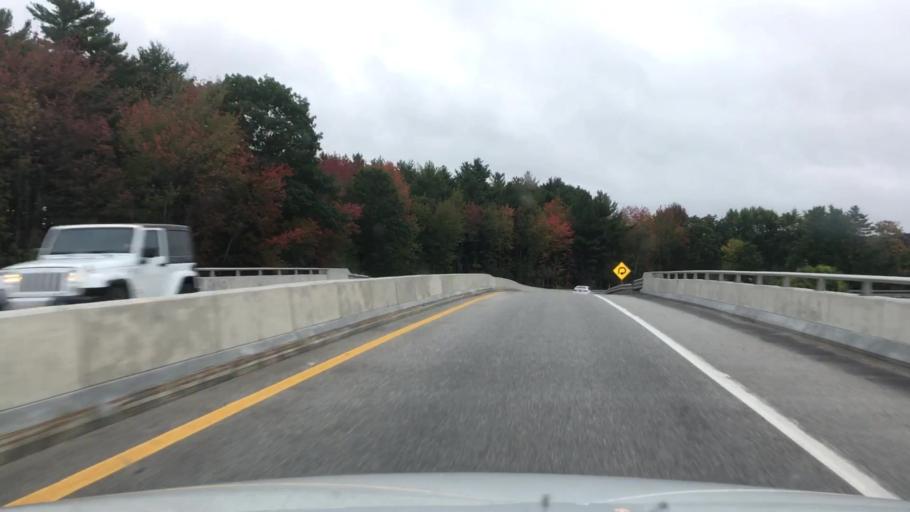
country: US
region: Maine
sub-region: Cumberland County
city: South Portland Gardens
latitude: 43.6807
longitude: -70.3251
